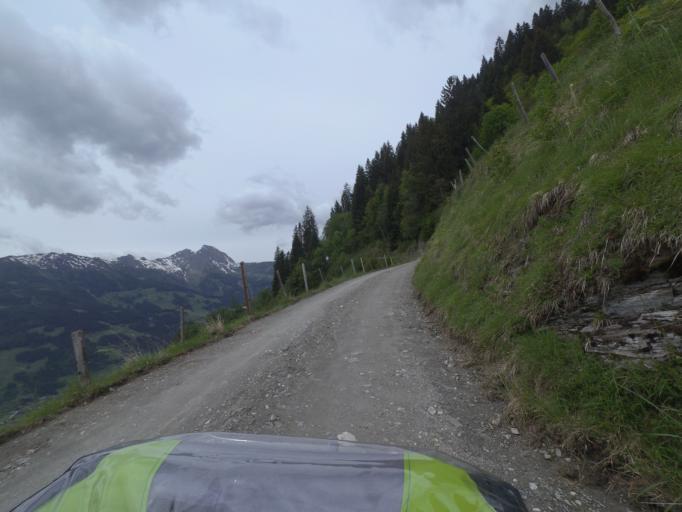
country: AT
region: Salzburg
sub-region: Politischer Bezirk Sankt Johann im Pongau
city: Dorfgastein
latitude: 47.2540
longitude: 13.1236
